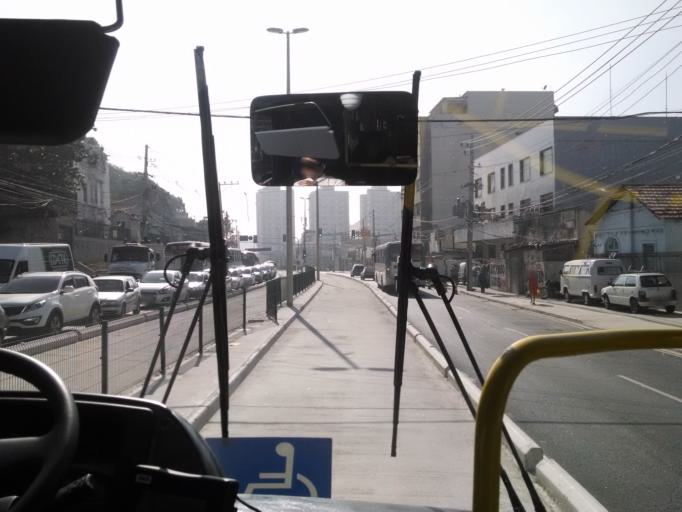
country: BR
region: Rio de Janeiro
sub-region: Sao Joao De Meriti
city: Sao Joao de Meriti
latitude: -22.8959
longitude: -43.3506
